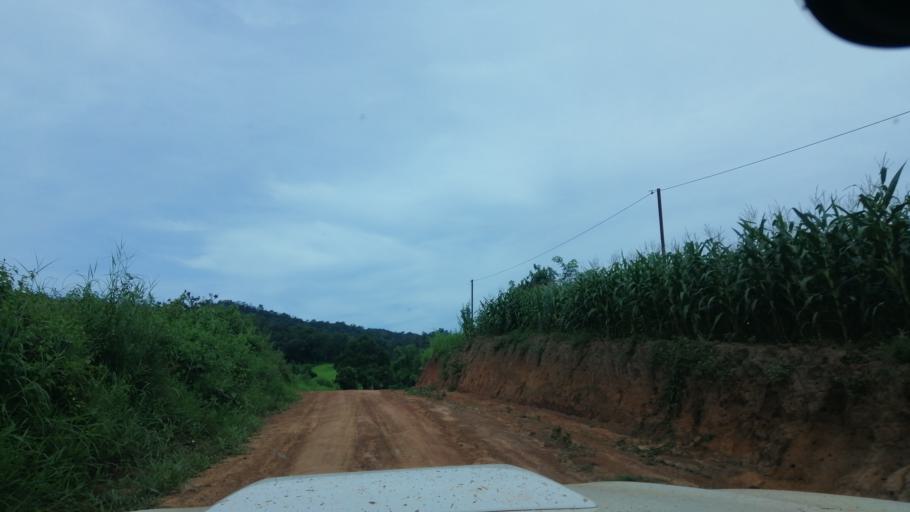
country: TH
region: Loei
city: Na Haeo
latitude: 17.5857
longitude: 101.1359
